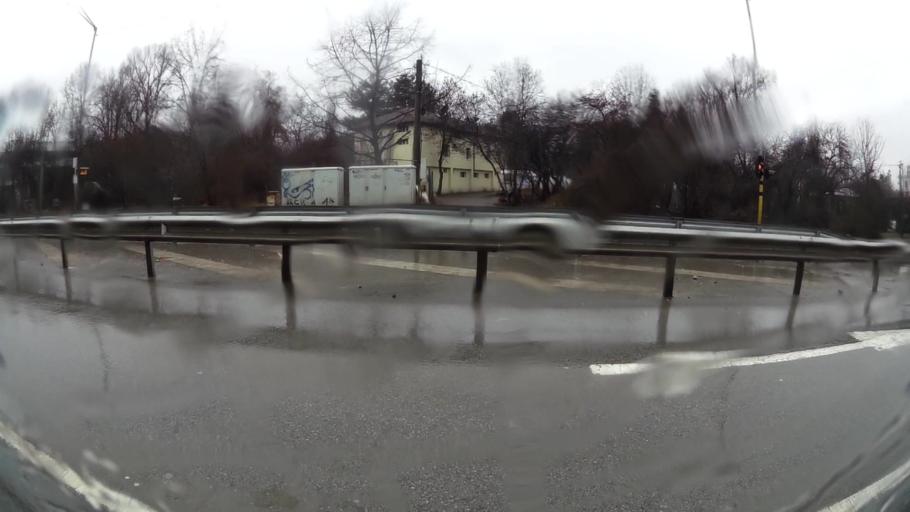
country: BG
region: Sofia-Capital
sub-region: Stolichna Obshtina
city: Sofia
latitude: 42.6573
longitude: 23.3365
